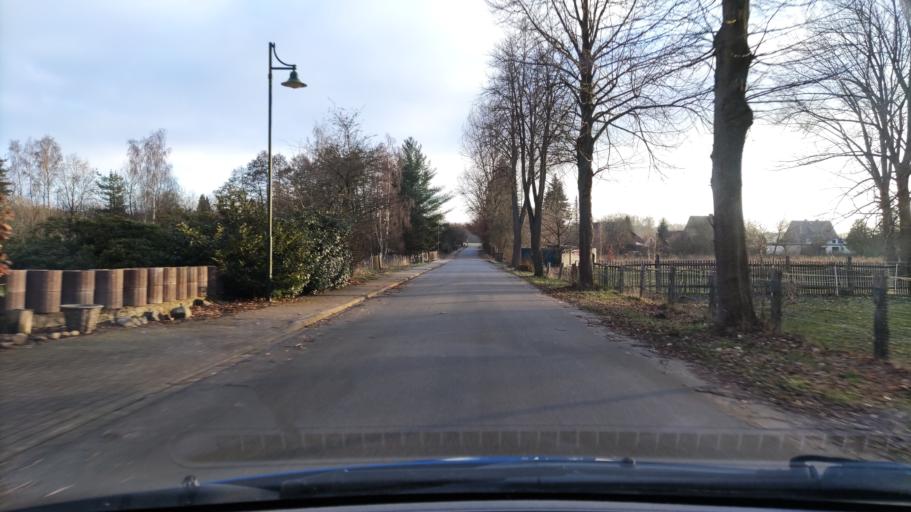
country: DE
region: Lower Saxony
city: Gerdau
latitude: 52.9704
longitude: 10.3967
